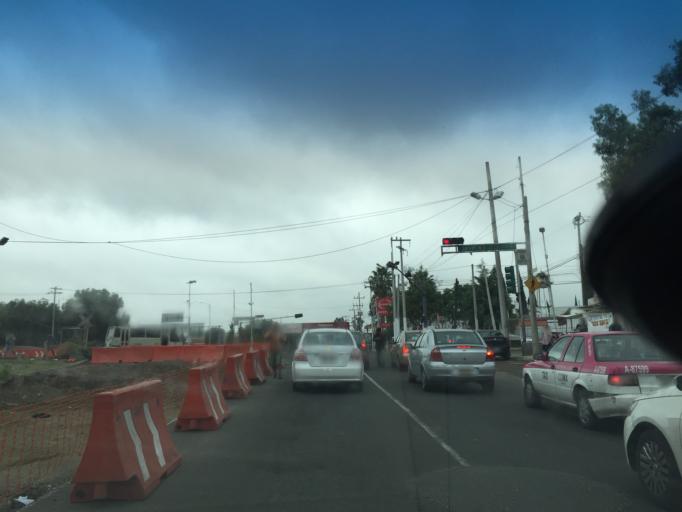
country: MX
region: Mexico City
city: Azcapotzalco
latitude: 19.5102
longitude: -99.1915
